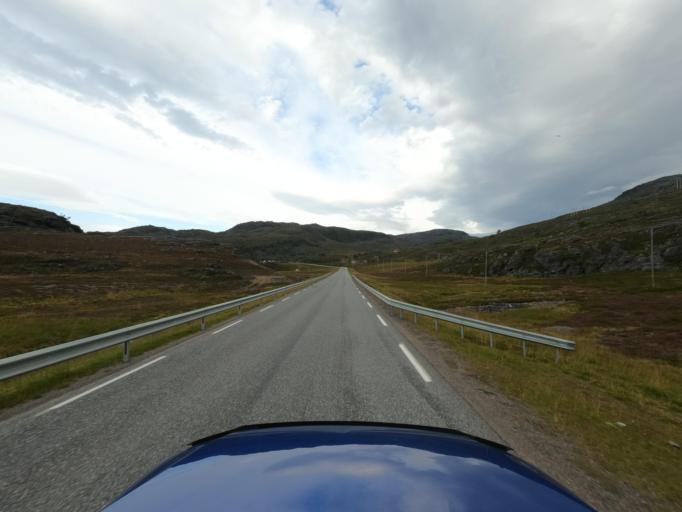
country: NO
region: Finnmark Fylke
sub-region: Hammerfest
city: Rypefjord
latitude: 70.5970
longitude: 23.6826
